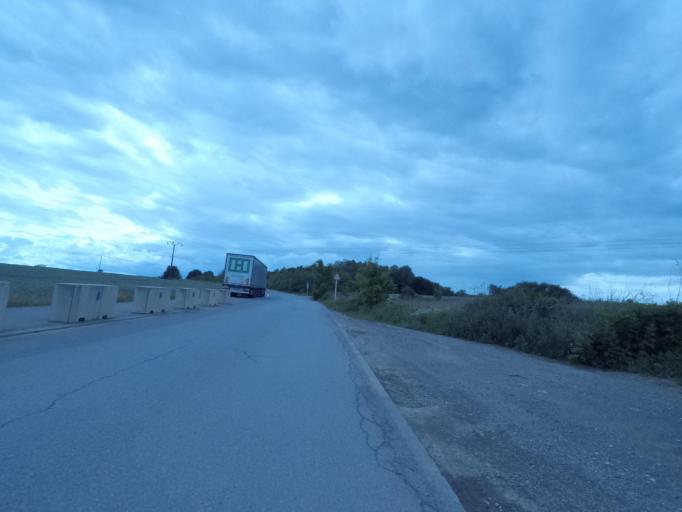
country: LU
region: Luxembourg
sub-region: Canton de Luxembourg
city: Strassen
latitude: 49.6132
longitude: 6.0883
